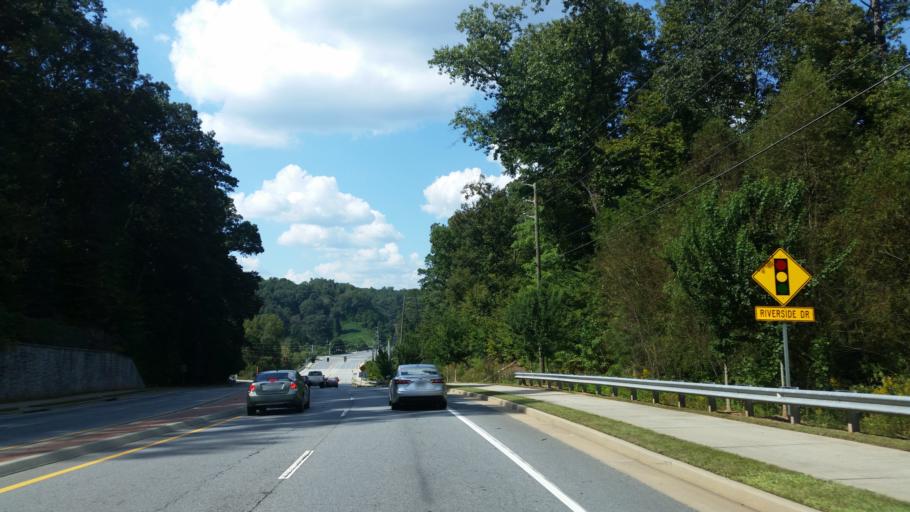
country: US
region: Georgia
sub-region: Fulton County
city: Sandy Springs
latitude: 33.9414
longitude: -84.4020
